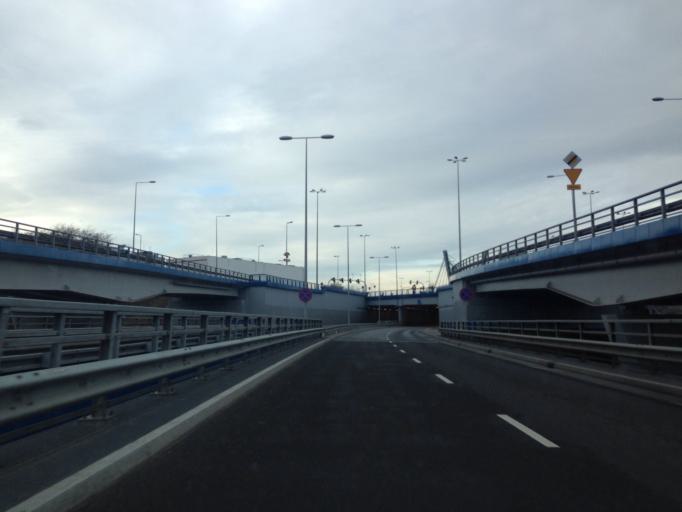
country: PL
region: Kujawsko-Pomorskie
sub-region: Torun
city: Torun
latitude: 53.0203
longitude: 18.6500
